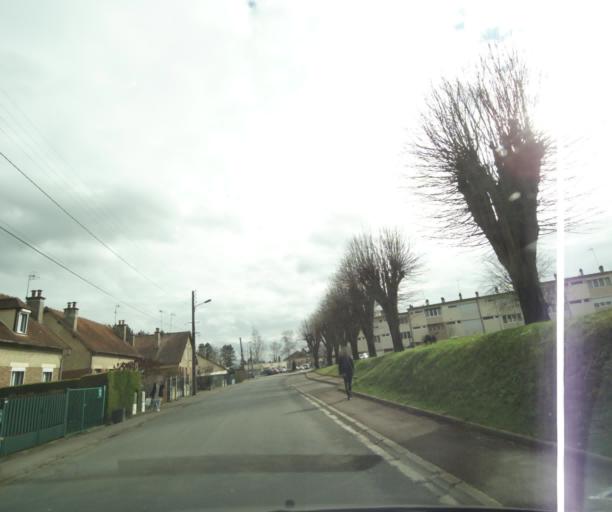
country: FR
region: Picardie
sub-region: Departement de l'Oise
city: Noyon
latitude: 49.5812
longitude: 2.9898
